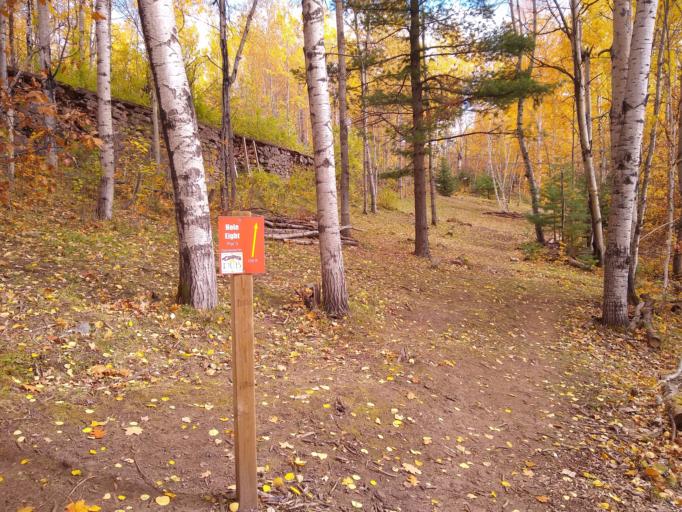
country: US
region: Michigan
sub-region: Marquette County
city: Negaunee
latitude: 46.5002
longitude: -87.6203
